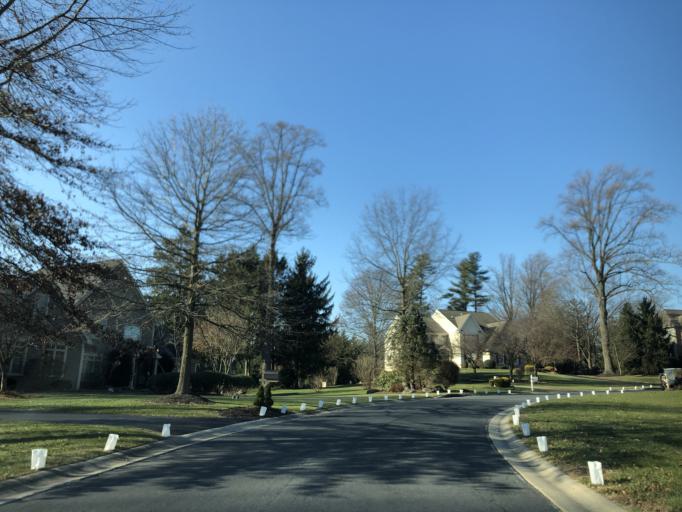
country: US
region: Pennsylvania
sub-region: Chester County
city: Downingtown
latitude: 39.9892
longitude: -75.7066
